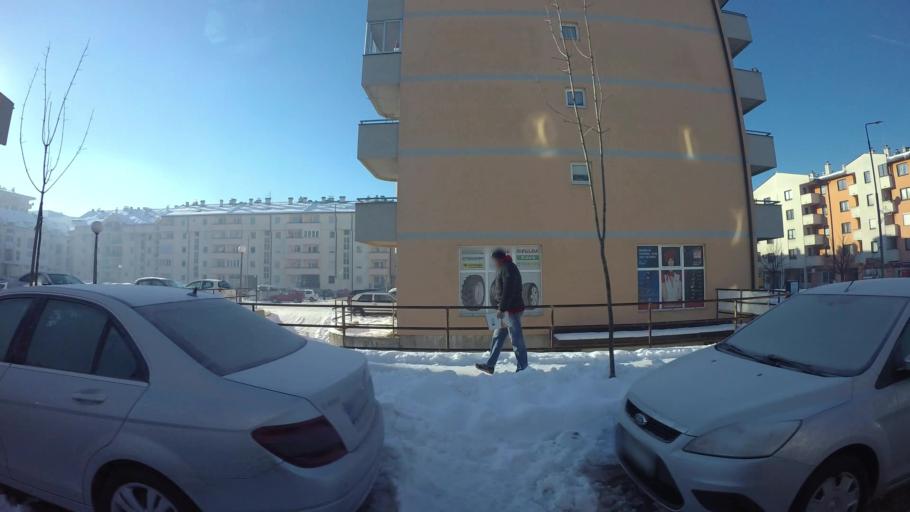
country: BA
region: Federation of Bosnia and Herzegovina
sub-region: Kanton Sarajevo
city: Sarajevo
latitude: 43.8211
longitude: 18.3640
